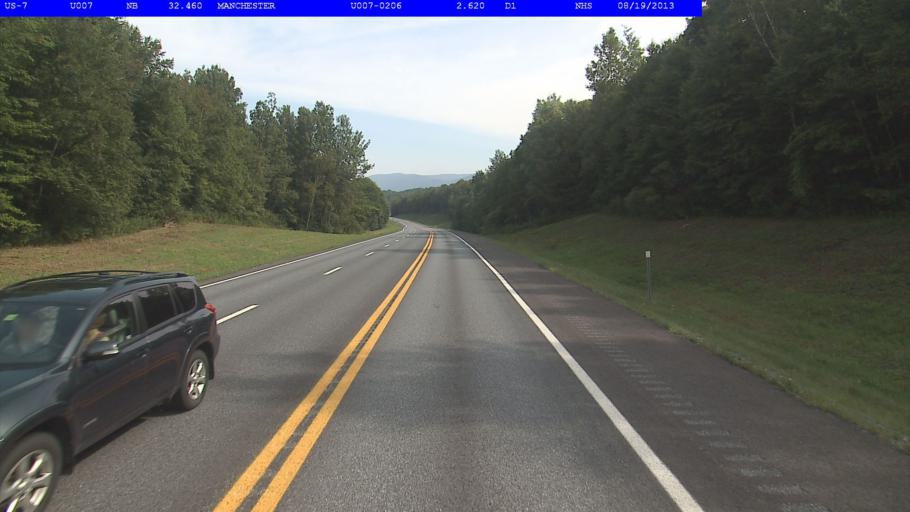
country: US
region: Vermont
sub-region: Bennington County
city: Manchester Center
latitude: 43.1477
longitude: -73.0489
